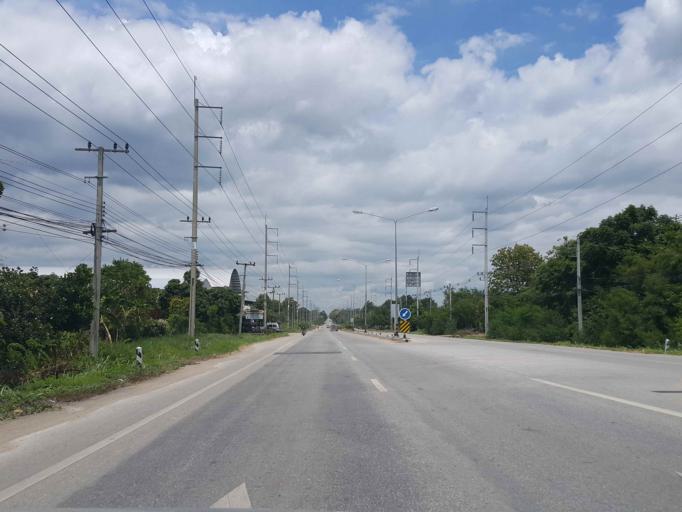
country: TH
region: Lamphun
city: Ban Hong
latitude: 18.3554
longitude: 98.8094
